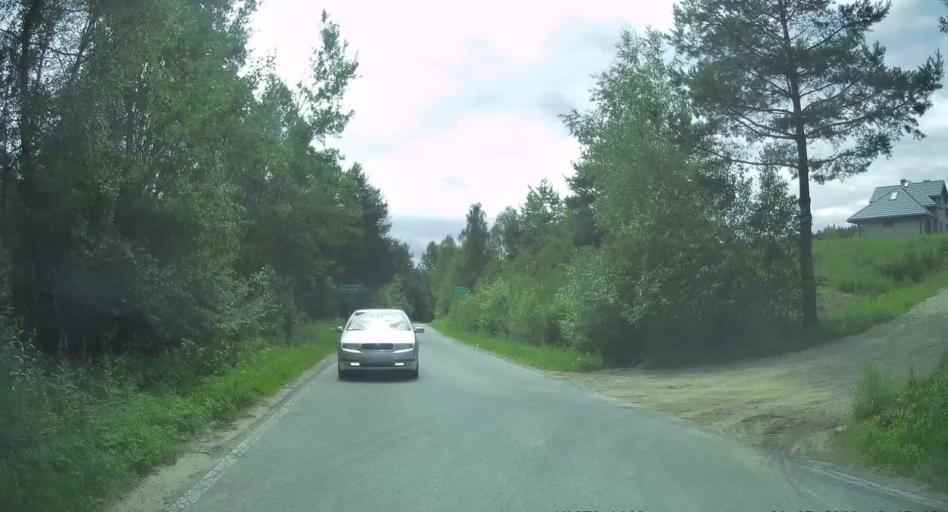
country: PL
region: Lesser Poland Voivodeship
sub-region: Powiat nowosadecki
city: Muszyna
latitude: 49.3865
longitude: 20.9022
